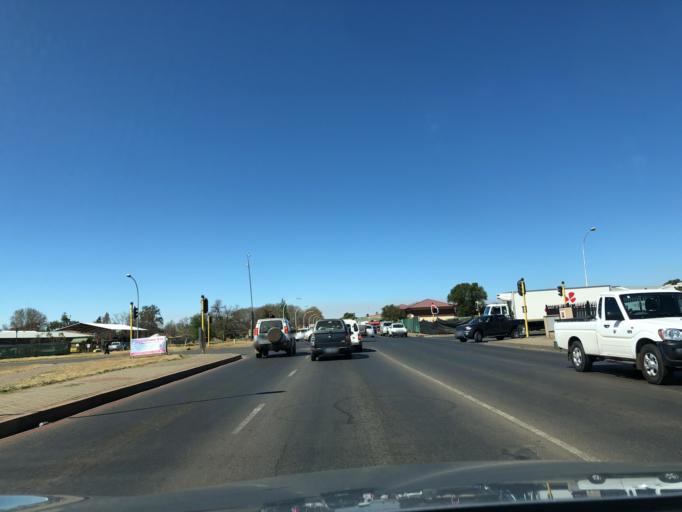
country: ZA
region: KwaZulu-Natal
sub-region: Amajuba District Municipality
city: Newcastle
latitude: -27.7538
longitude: 29.9396
